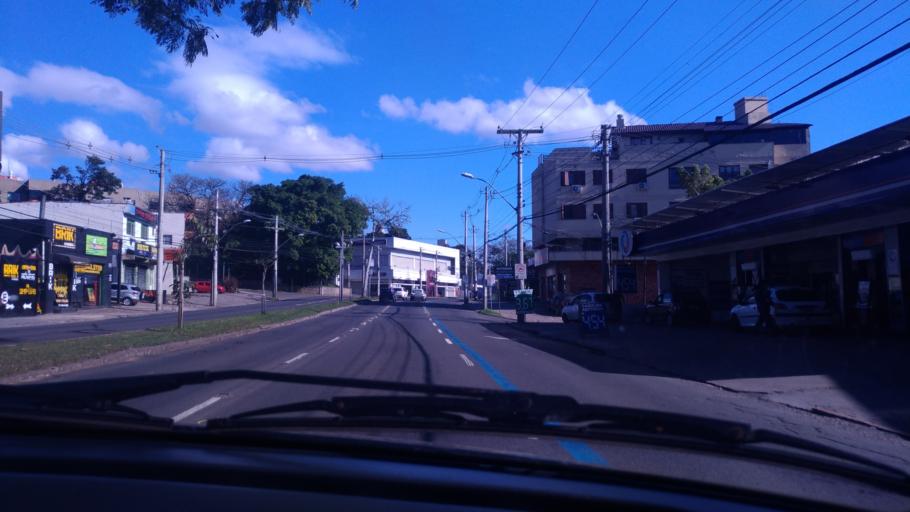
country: BR
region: Rio Grande do Sul
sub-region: Porto Alegre
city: Porto Alegre
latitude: -30.0905
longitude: -51.2194
